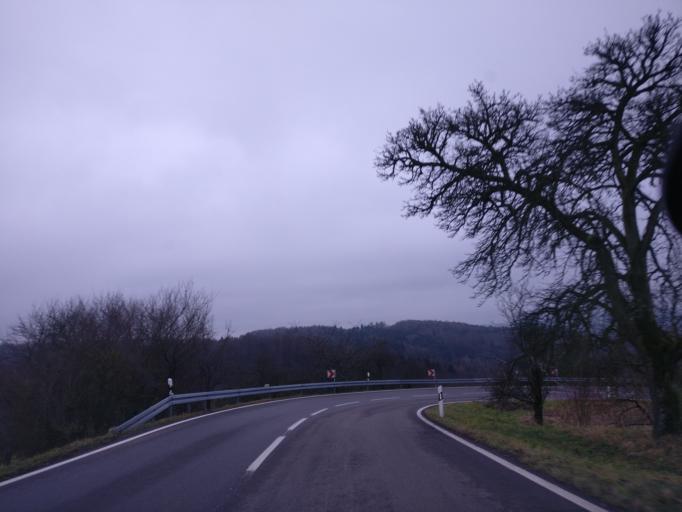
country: DE
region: Baden-Wuerttemberg
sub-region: Regierungsbezirk Stuttgart
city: Rudersberg
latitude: 48.8629
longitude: 9.4969
